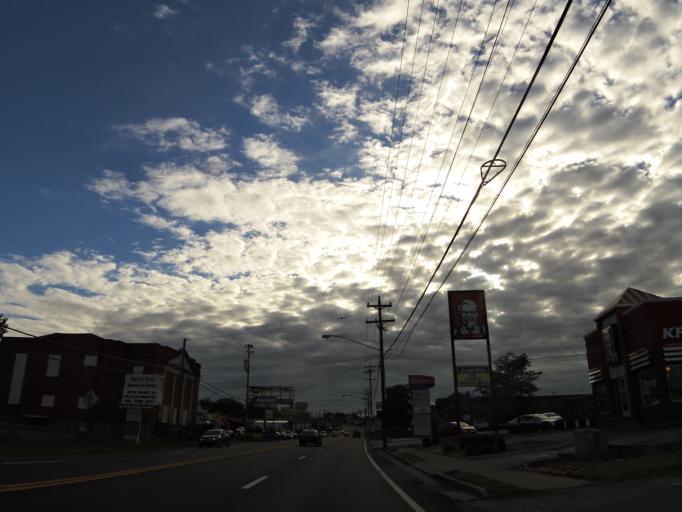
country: US
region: Tennessee
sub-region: Davidson County
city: Belle Meade
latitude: 36.1478
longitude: -86.8669
